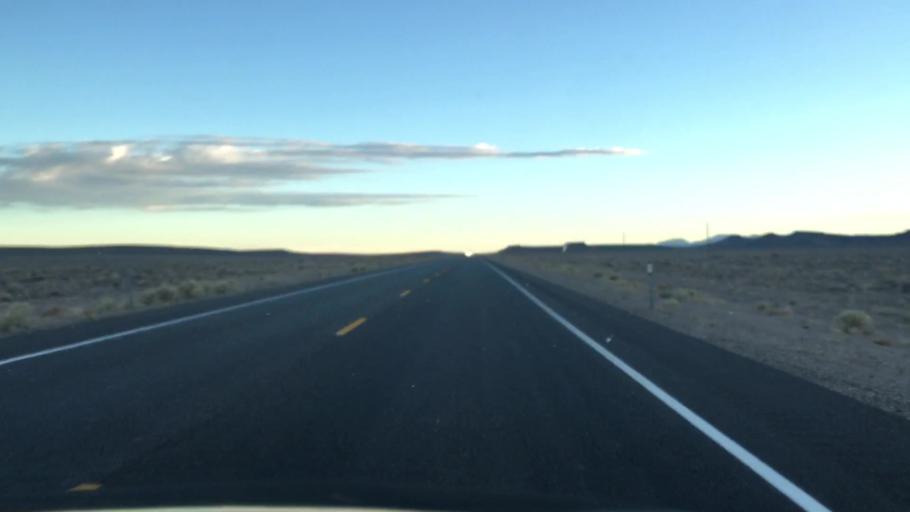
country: US
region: Nevada
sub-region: Esmeralda County
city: Goldfield
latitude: 37.4221
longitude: -117.1573
